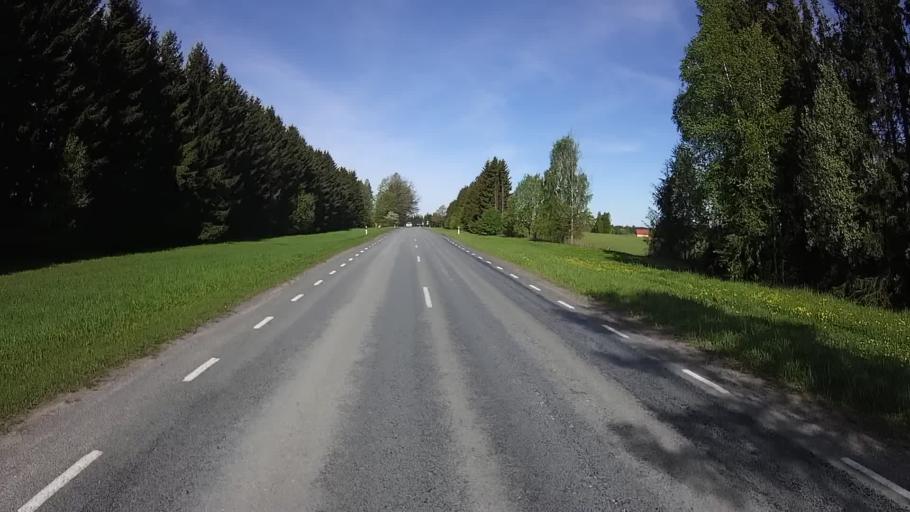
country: EE
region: Polvamaa
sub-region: Polva linn
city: Polva
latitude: 58.2247
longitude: 27.0363
